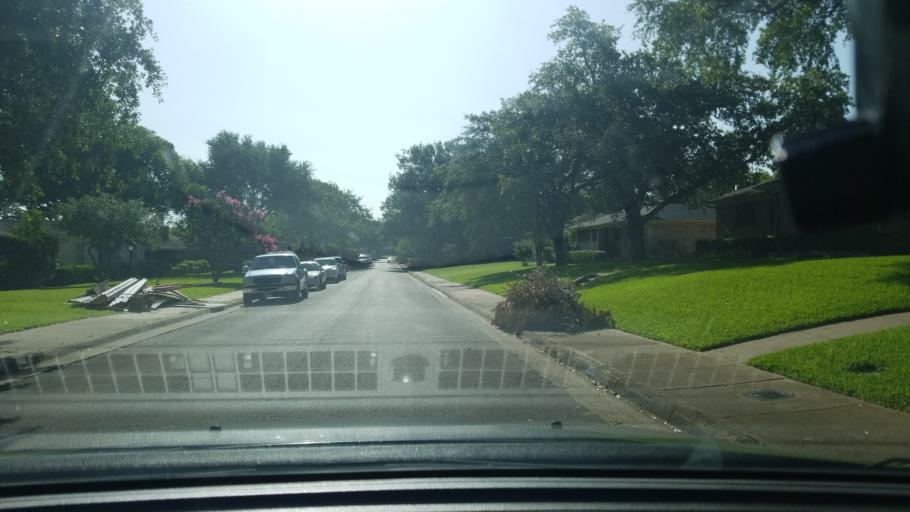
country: US
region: Texas
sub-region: Dallas County
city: Mesquite
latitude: 32.8093
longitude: -96.6777
